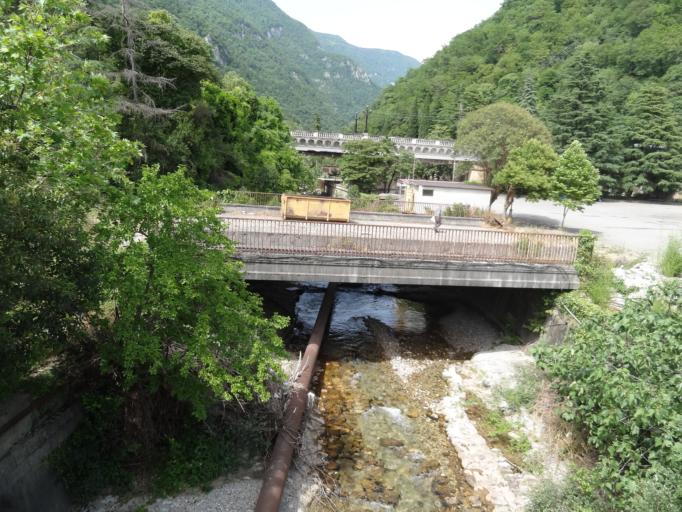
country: GE
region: Abkhazia
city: Gagra
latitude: 43.3264
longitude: 40.2224
